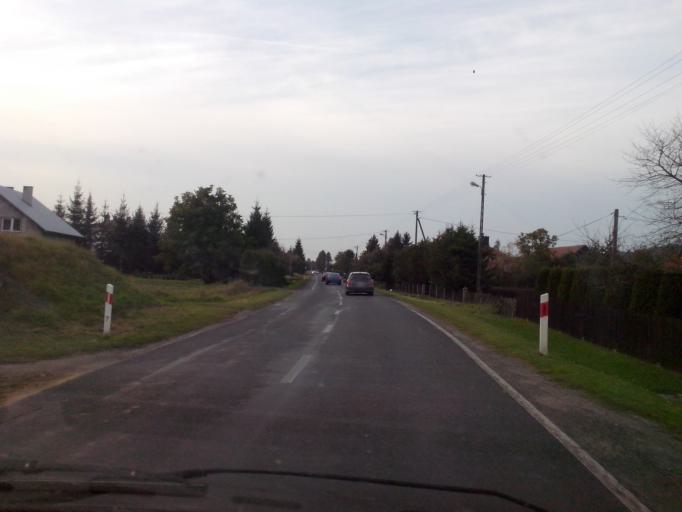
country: PL
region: Subcarpathian Voivodeship
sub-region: Powiat strzyzowski
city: Strzyzow
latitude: 49.8384
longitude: 21.8227
